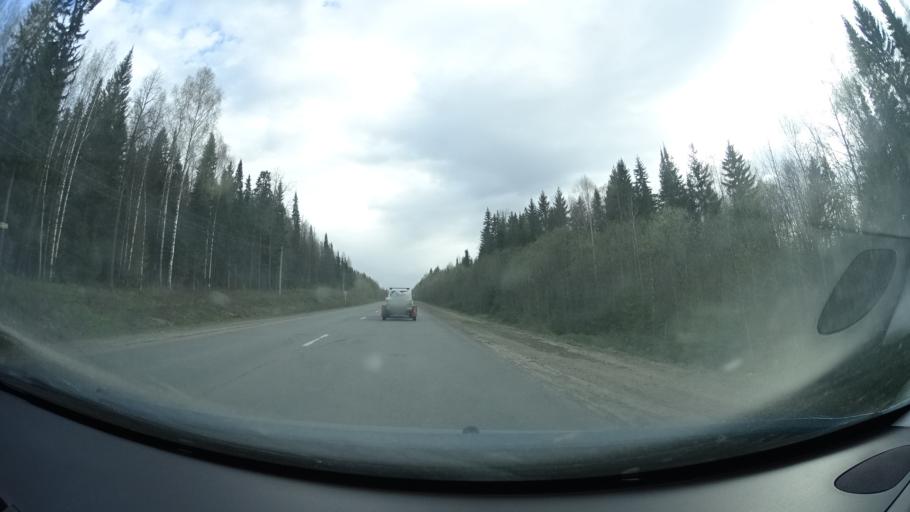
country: RU
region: Perm
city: Kultayevo
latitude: 57.7971
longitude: 55.7794
